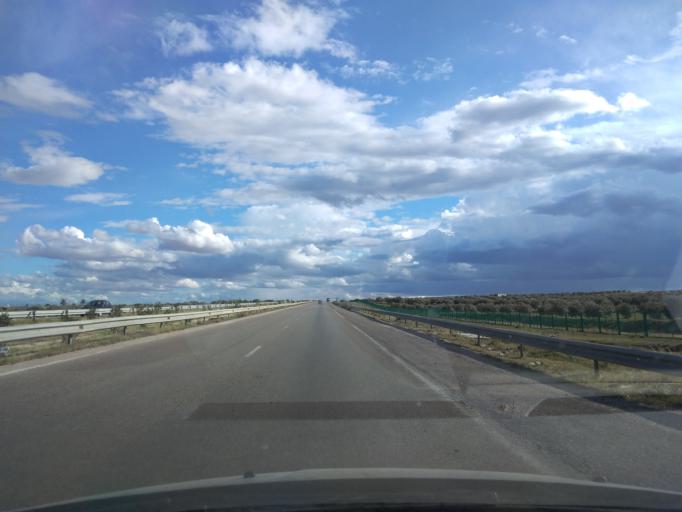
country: TN
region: Al Munastir
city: Manzil Kamil
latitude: 35.5552
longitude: 10.6181
